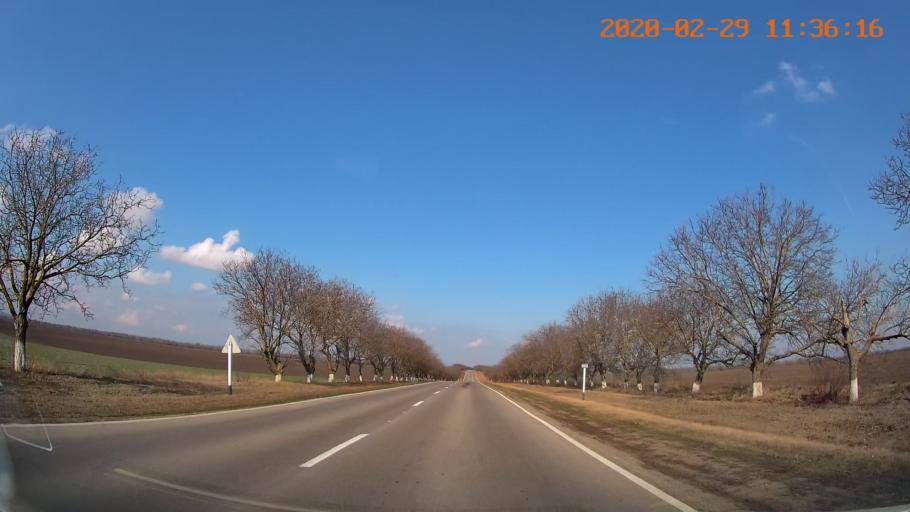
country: MD
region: Rezina
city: Saharna
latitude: 47.5934
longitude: 29.0575
